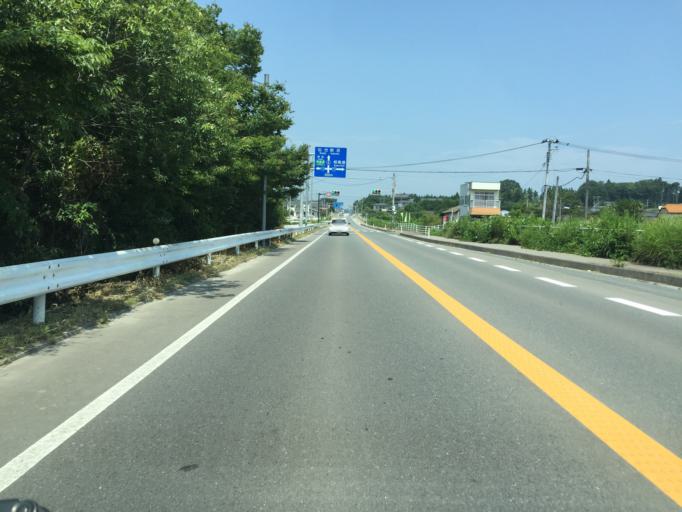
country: JP
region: Miyagi
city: Marumori
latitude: 37.8326
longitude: 140.9184
